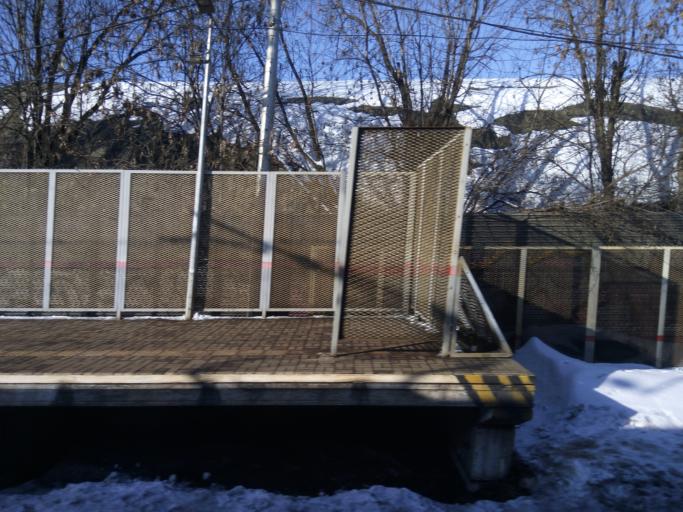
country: RU
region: Moskovskaya
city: Vostochnoe Degunino
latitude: 55.8835
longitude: 37.5672
